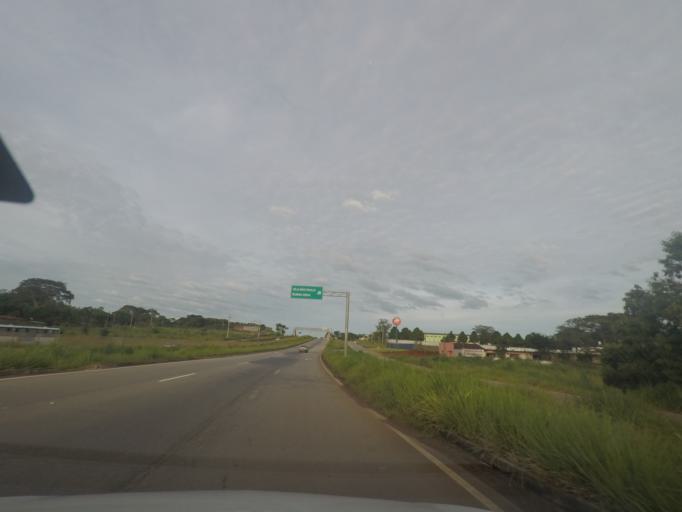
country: BR
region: Goias
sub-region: Trindade
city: Trindade
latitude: -16.7310
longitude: -49.3928
